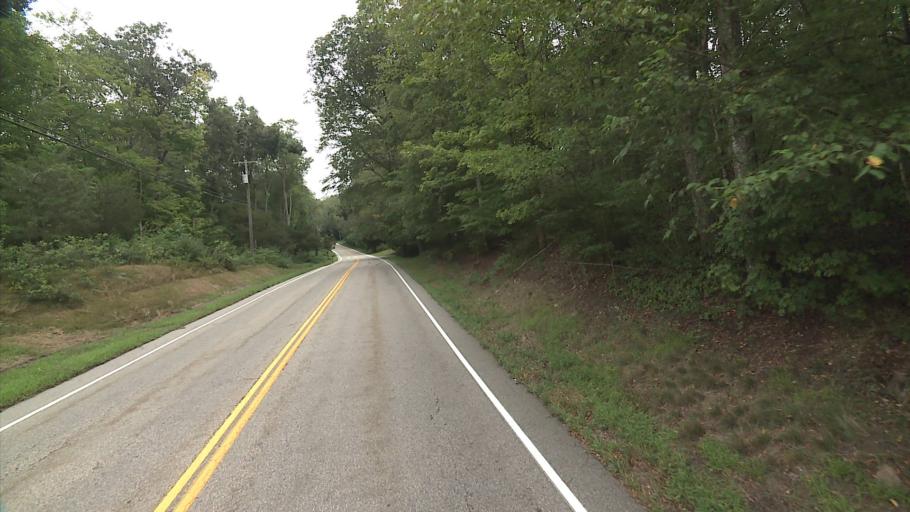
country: US
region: Connecticut
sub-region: Middlesex County
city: Essex Village
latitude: 41.4164
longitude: -72.3350
